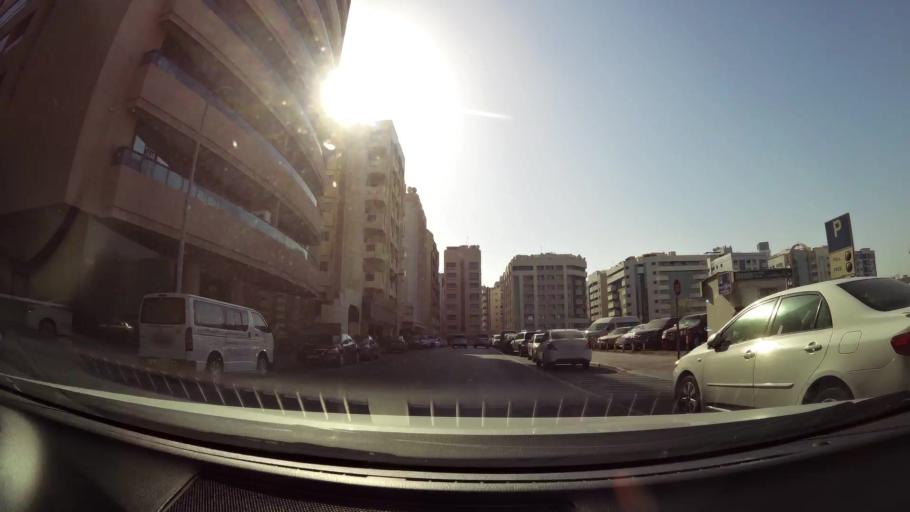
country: AE
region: Ash Shariqah
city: Sharjah
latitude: 25.2568
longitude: 55.2881
